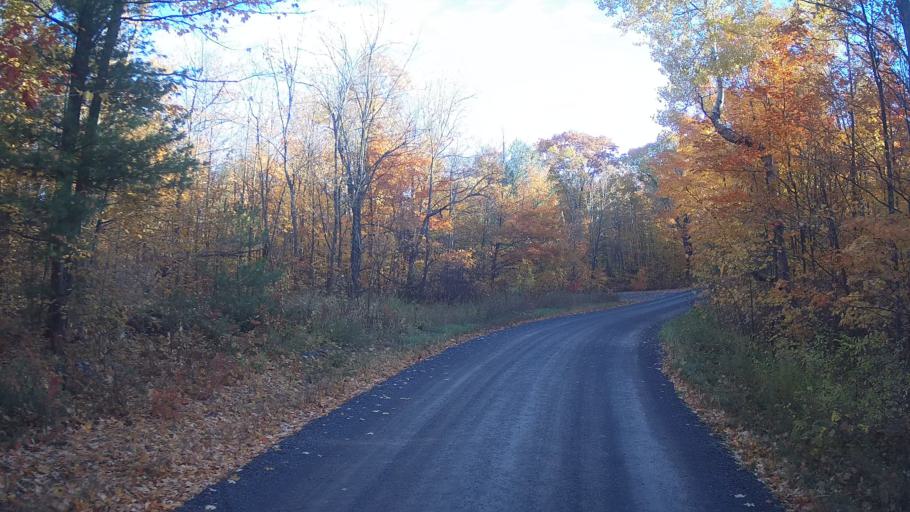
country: CA
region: Ontario
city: Arnprior
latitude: 45.3425
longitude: -76.3456
